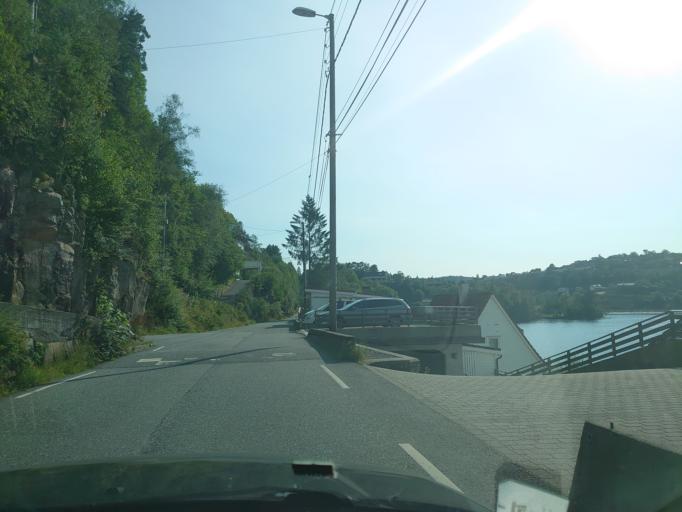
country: NO
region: Hordaland
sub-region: Bergen
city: Ytrebygda
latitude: 60.3310
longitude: 5.2829
